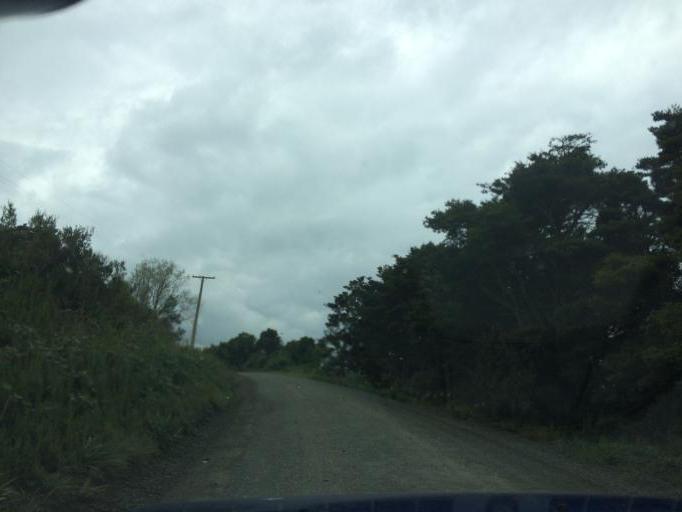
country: NZ
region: Northland
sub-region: Kaipara District
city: Dargaville
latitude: -35.8241
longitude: 173.8441
